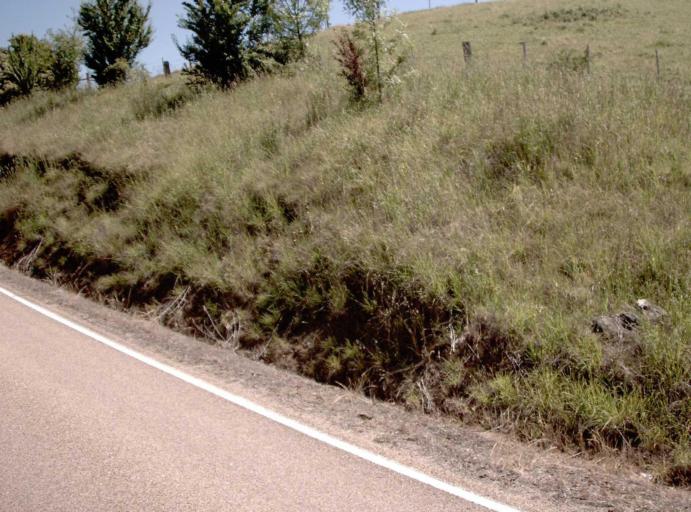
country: AU
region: Victoria
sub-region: East Gippsland
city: Lakes Entrance
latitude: -37.4923
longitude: 148.1728
